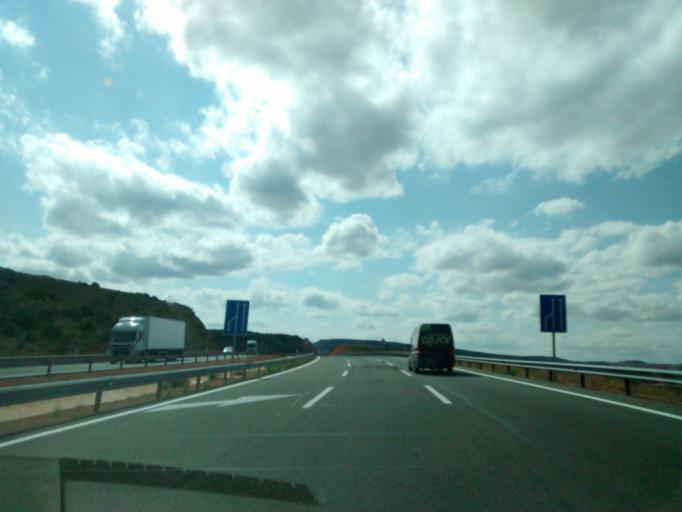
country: ES
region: Castille and Leon
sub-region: Provincia de Soria
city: Arcos de Jalon
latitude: 41.2020
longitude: -2.3238
